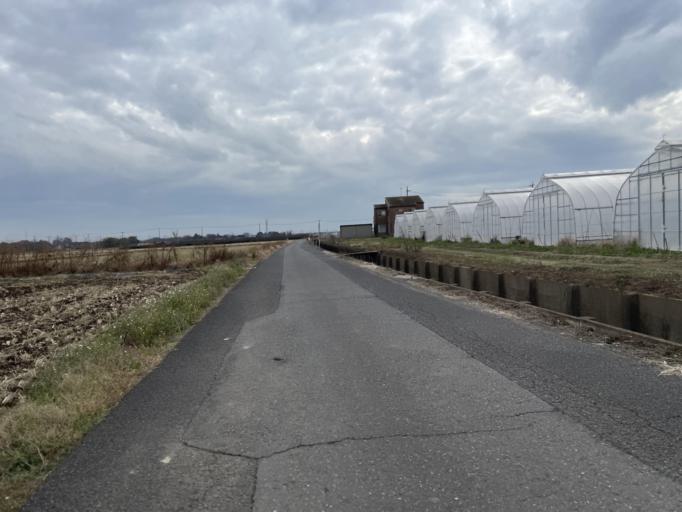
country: JP
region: Saitama
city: Shiraoka
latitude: 36.0270
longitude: 139.6455
